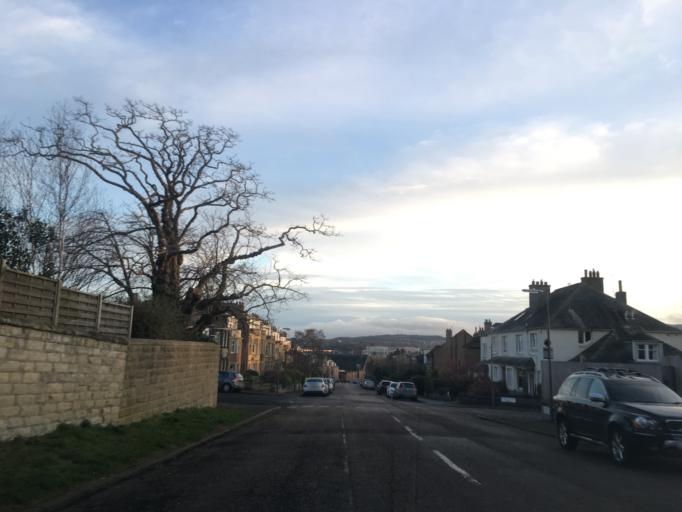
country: GB
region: Scotland
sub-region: Edinburgh
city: Colinton
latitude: 55.9482
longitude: -3.2437
